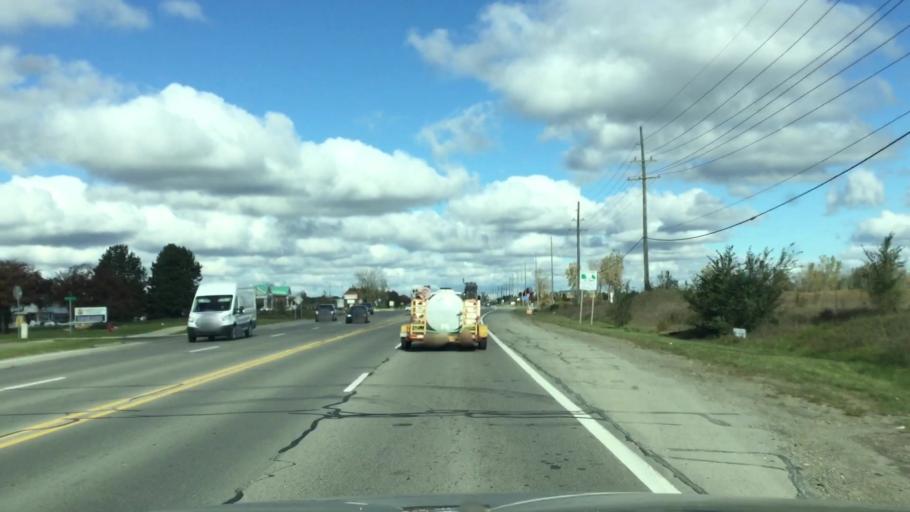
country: US
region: Michigan
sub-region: Oakland County
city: Oxford
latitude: 42.8312
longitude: -83.2696
